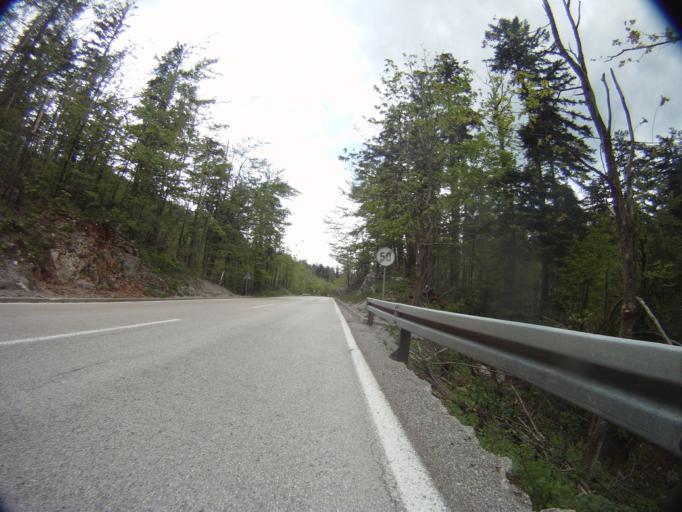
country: HR
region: Primorsko-Goranska
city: Hreljin
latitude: 45.3429
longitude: 14.6909
